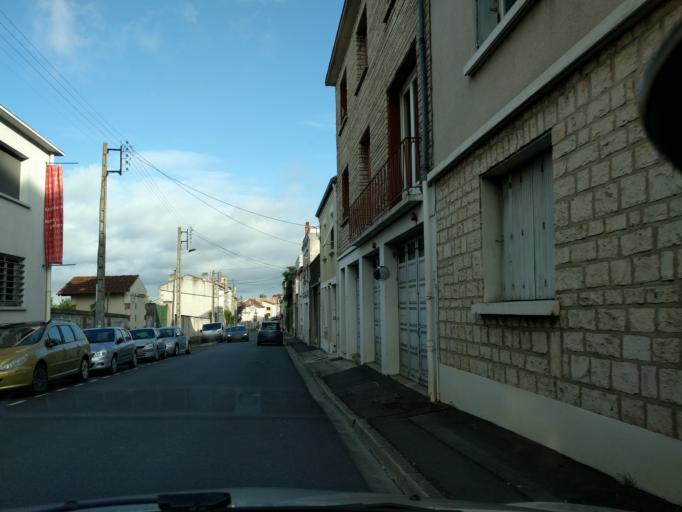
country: FR
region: Poitou-Charentes
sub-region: Departement de la Charente
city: Angouleme
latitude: 45.6453
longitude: 0.1539
